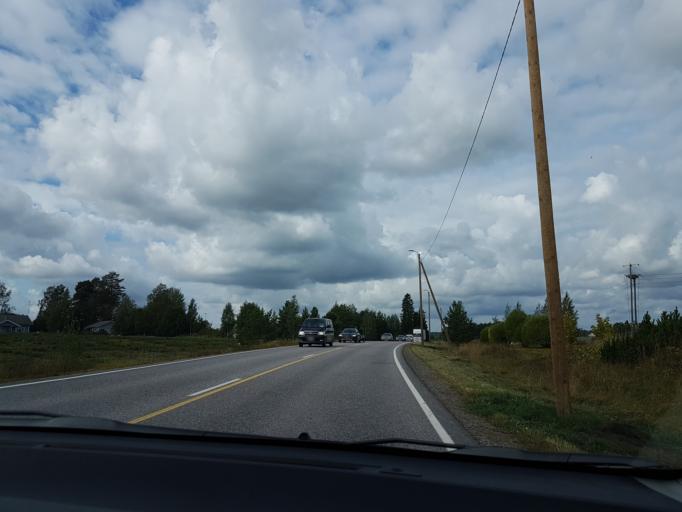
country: FI
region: Uusimaa
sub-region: Helsinki
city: Pornainen
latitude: 60.4856
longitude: 25.3586
